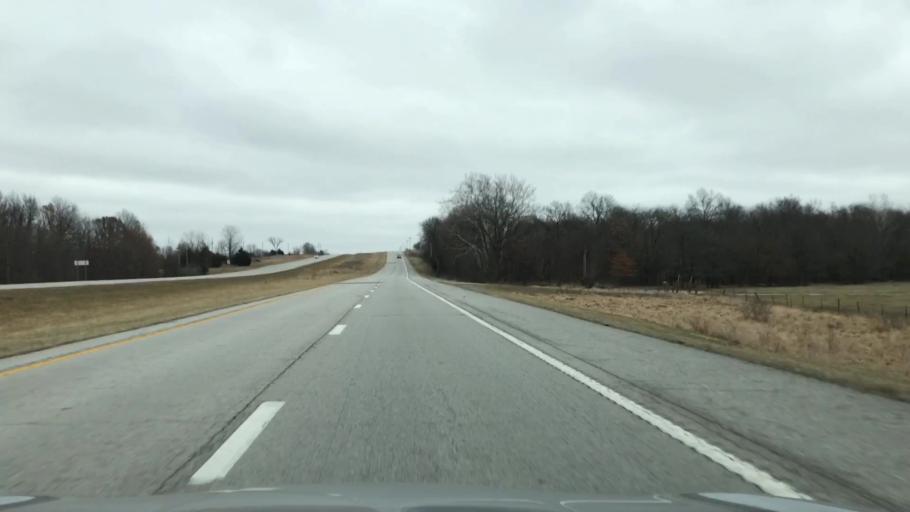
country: US
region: Missouri
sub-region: Linn County
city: Linneus
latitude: 39.7779
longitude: -93.2080
